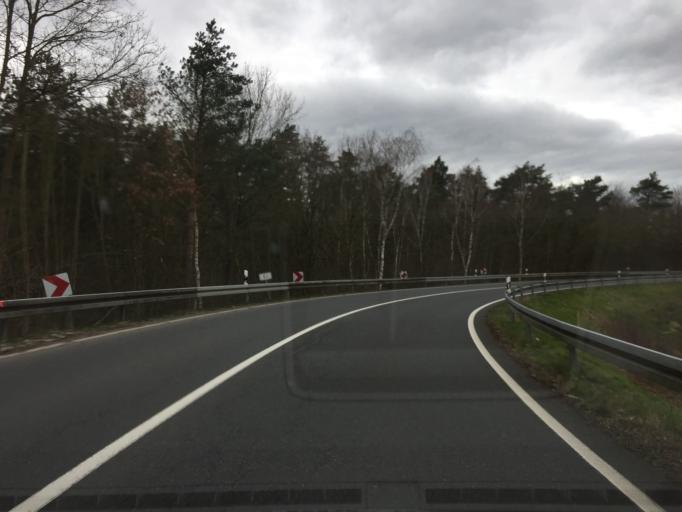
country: DE
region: Lower Saxony
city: Neustadt am Rubenberge
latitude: 52.4877
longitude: 9.4879
